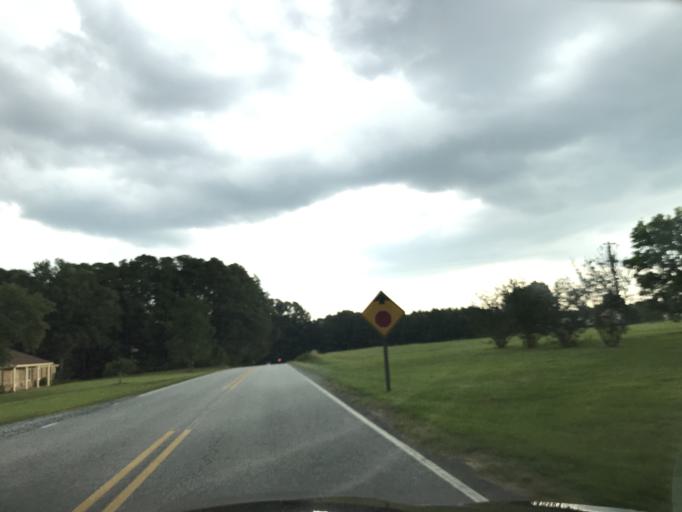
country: US
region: North Carolina
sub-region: Johnston County
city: Wilsons Mills
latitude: 35.5422
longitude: -78.4084
